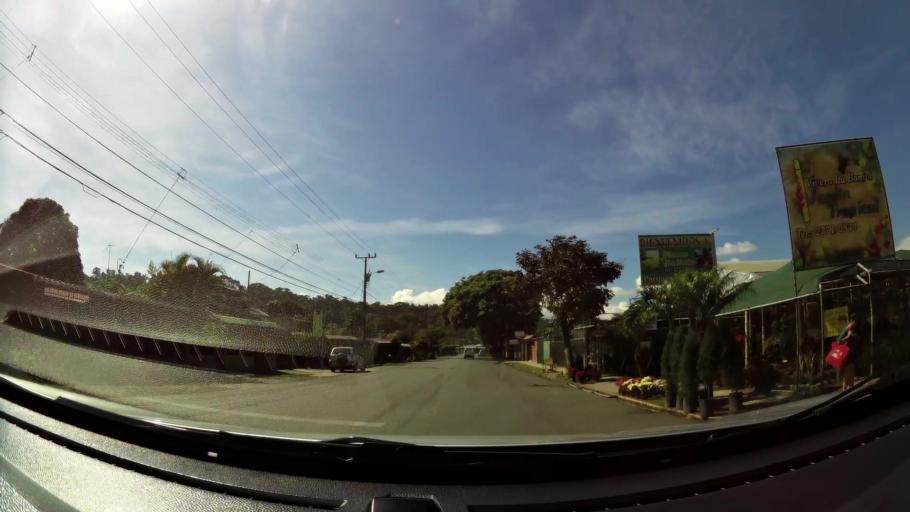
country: CR
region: San Jose
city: San Isidro
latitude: 9.3669
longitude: -83.7058
